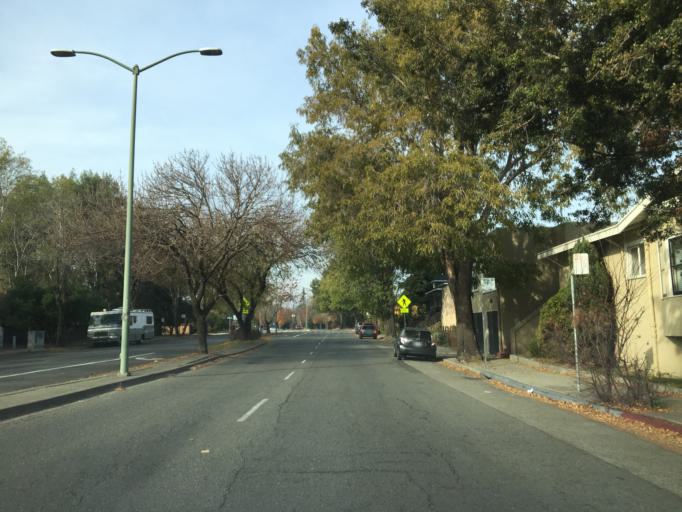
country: US
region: California
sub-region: Alameda County
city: Piedmont
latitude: 37.8359
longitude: -122.2552
